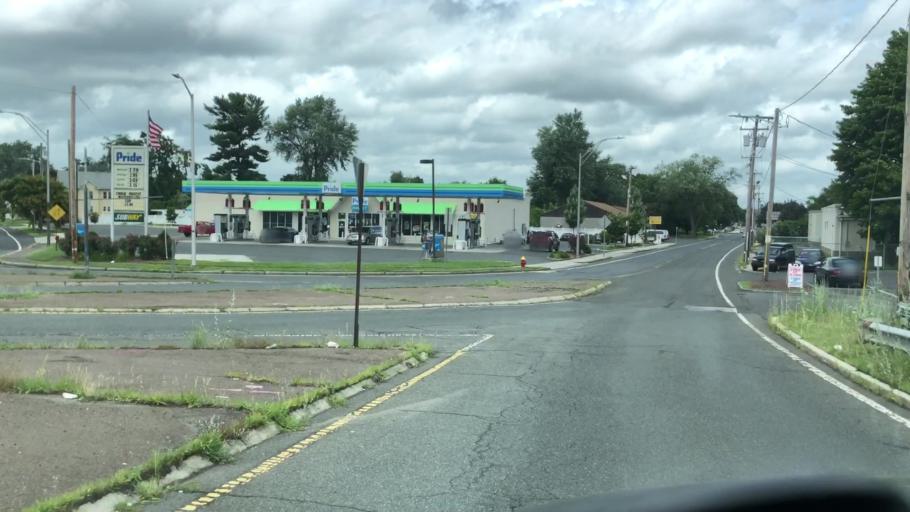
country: US
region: Massachusetts
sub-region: Hampden County
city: Chicopee
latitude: 42.1604
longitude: -72.6136
